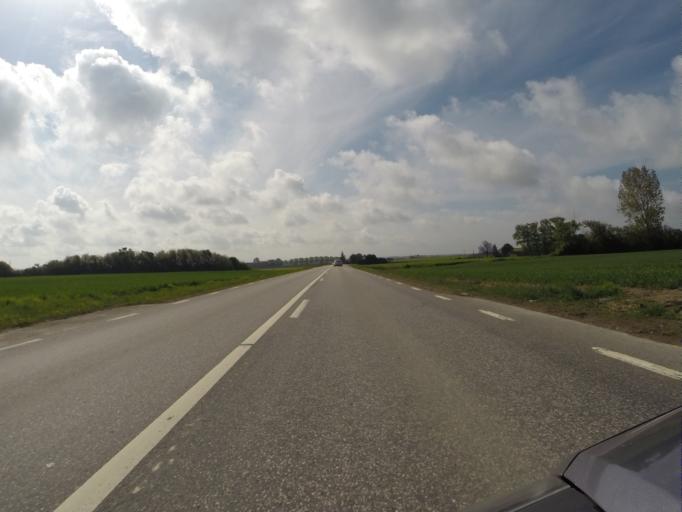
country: SE
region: Skane
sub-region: Landskrona
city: Asmundtorp
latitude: 55.9169
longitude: 12.9553
